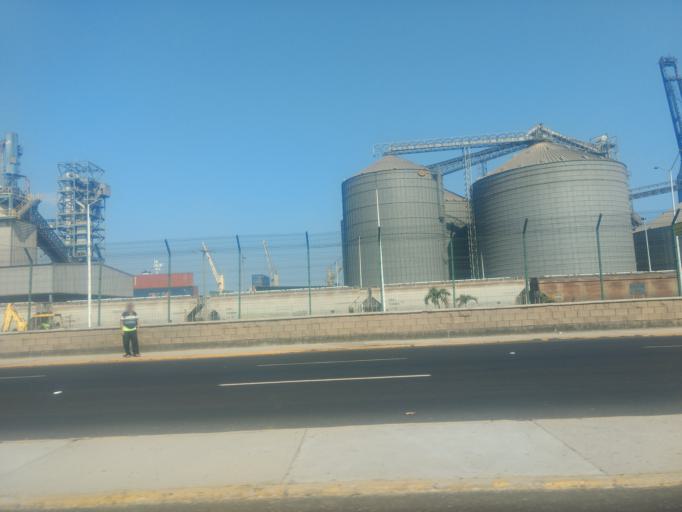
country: MX
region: Colima
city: Tapeixtles
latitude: 19.0637
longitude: -104.2897
